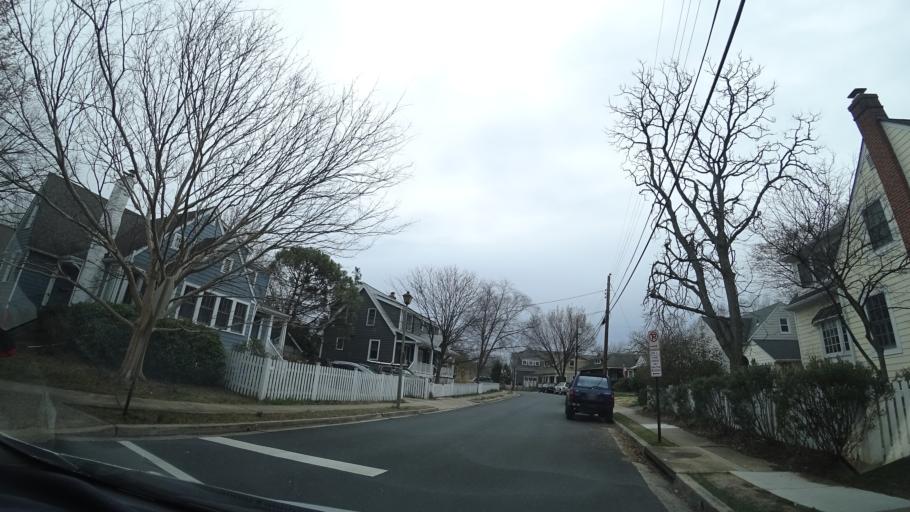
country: US
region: Virginia
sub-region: Arlington County
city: Arlington
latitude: 38.8925
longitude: -77.0910
